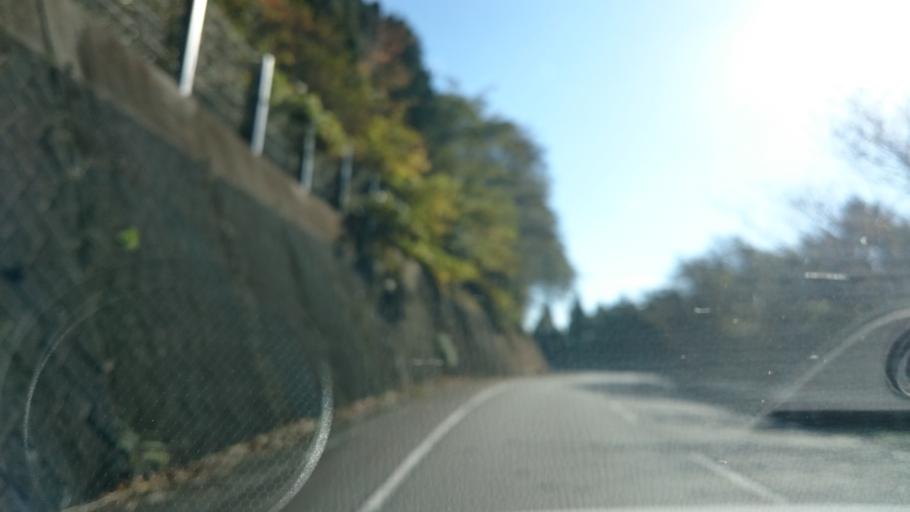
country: JP
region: Shizuoka
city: Heda
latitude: 34.9821
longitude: 138.8103
